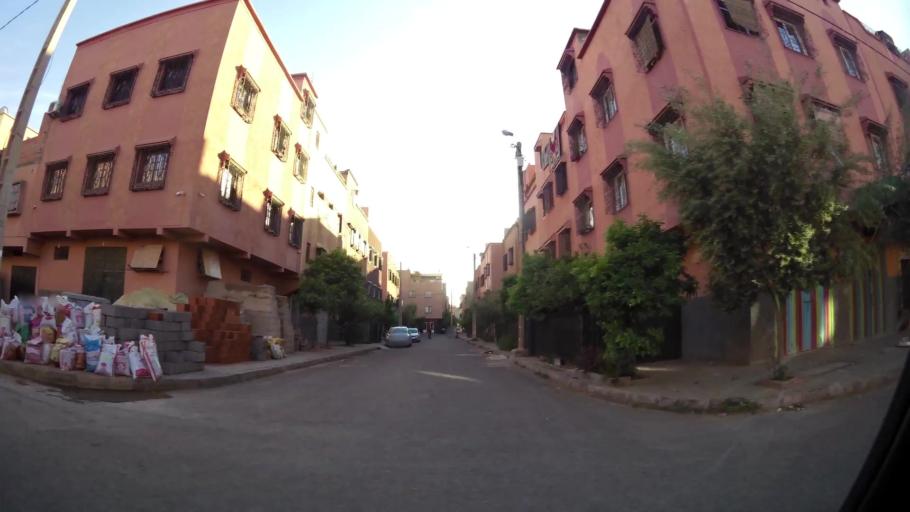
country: MA
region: Marrakech-Tensift-Al Haouz
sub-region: Marrakech
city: Marrakesh
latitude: 31.6172
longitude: -8.0558
